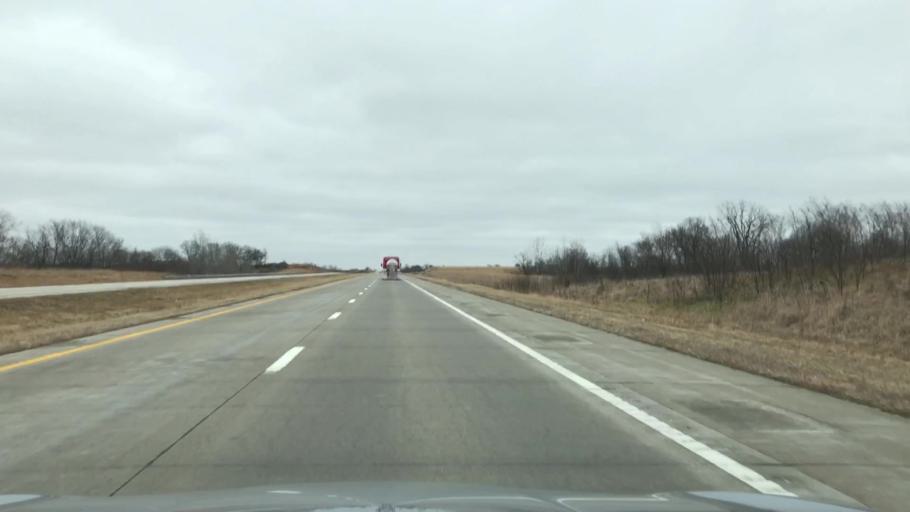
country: US
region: Missouri
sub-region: Caldwell County
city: Hamilton
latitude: 39.7346
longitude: -93.9551
